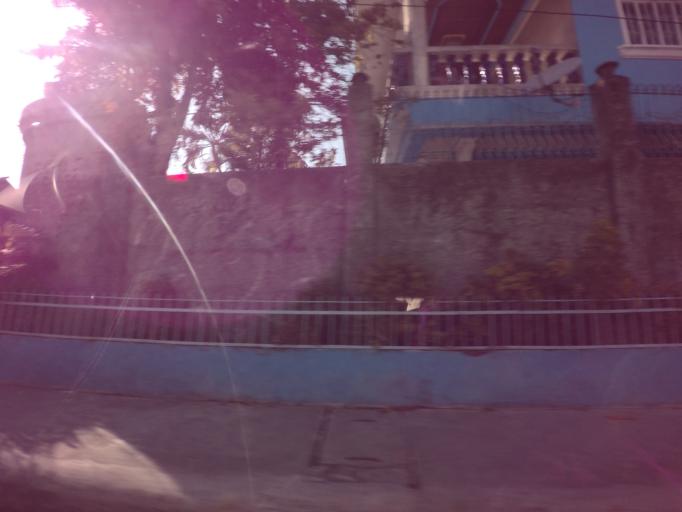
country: PH
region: Calabarzon
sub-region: Province of Rizal
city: Taguig
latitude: 14.4952
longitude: 121.0536
